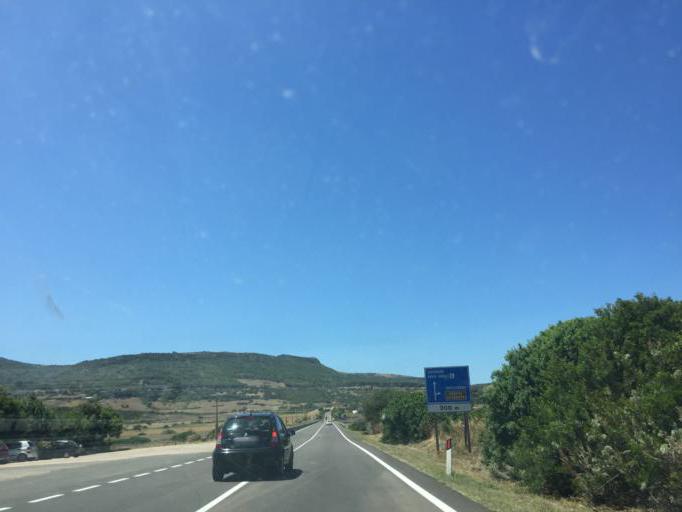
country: IT
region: Sardinia
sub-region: Provincia di Sassari
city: Castelsardo
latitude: 40.8989
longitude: 8.7667
